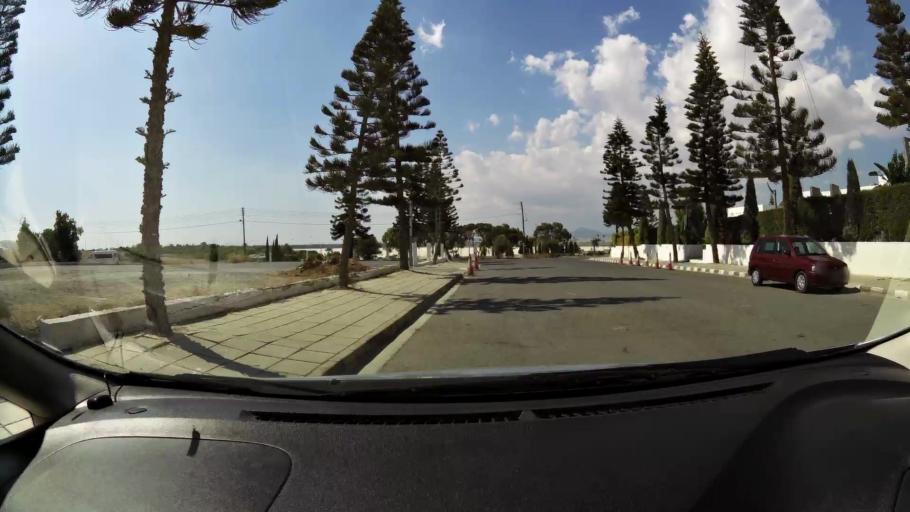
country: CY
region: Larnaka
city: Larnaca
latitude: 34.8942
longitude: 33.6342
